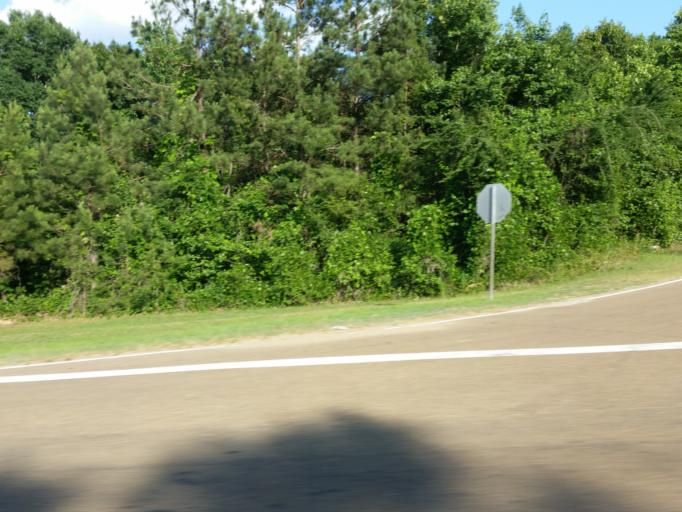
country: US
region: Mississippi
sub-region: Calhoun County
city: Calhoun City
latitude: 33.8023
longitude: -89.3544
